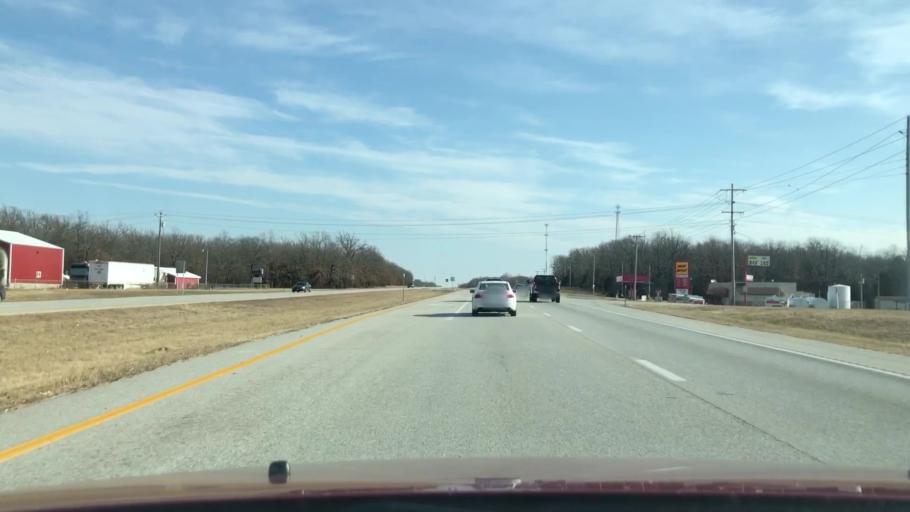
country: US
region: Missouri
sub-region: Webster County
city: Rogersville
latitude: 37.1162
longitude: -93.0255
